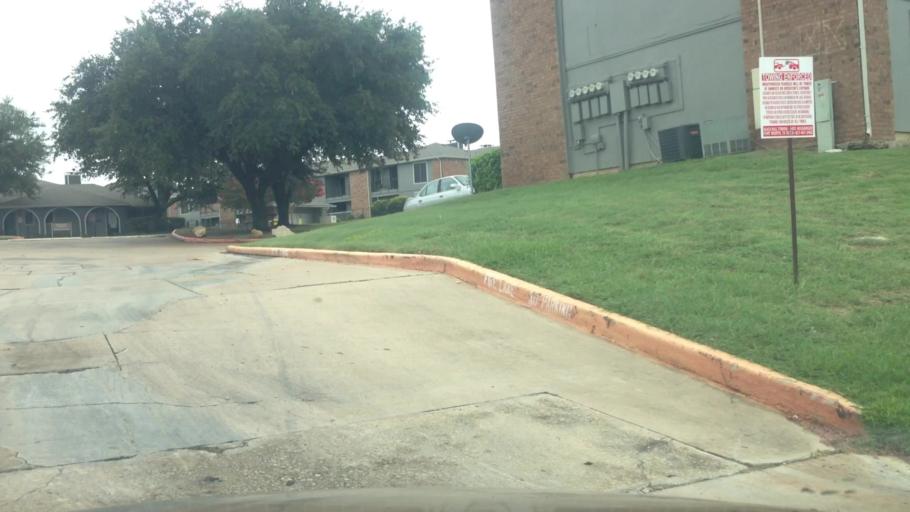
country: US
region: Texas
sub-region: Tarrant County
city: White Settlement
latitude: 32.7430
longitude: -97.4672
